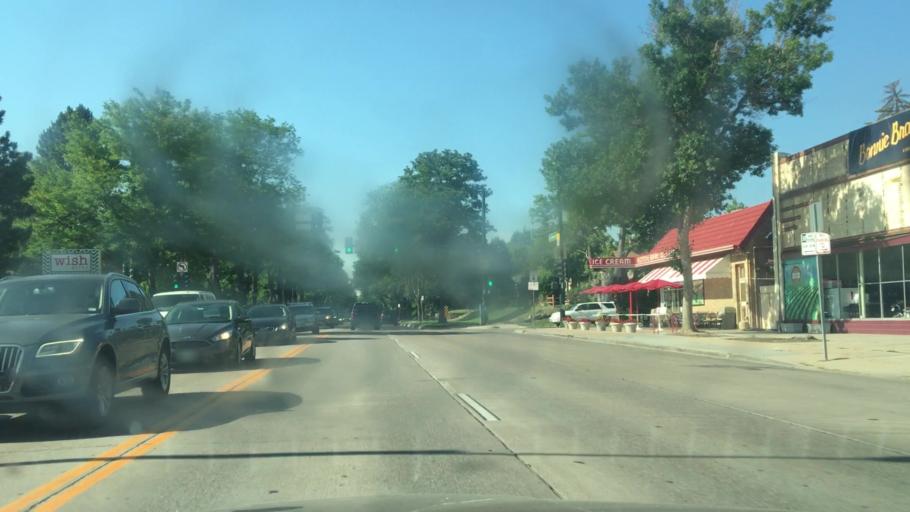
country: US
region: Colorado
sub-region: Arapahoe County
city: Glendale
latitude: 39.7025
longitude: -104.9594
